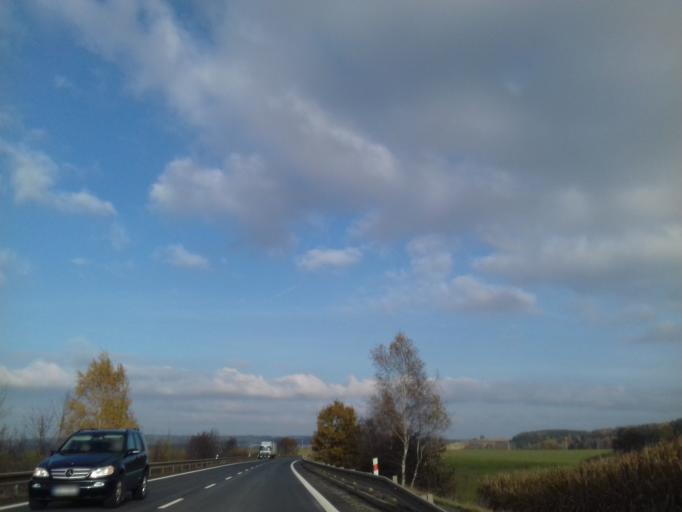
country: CZ
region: Plzensky
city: Meclov
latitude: 49.5089
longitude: 12.8989
